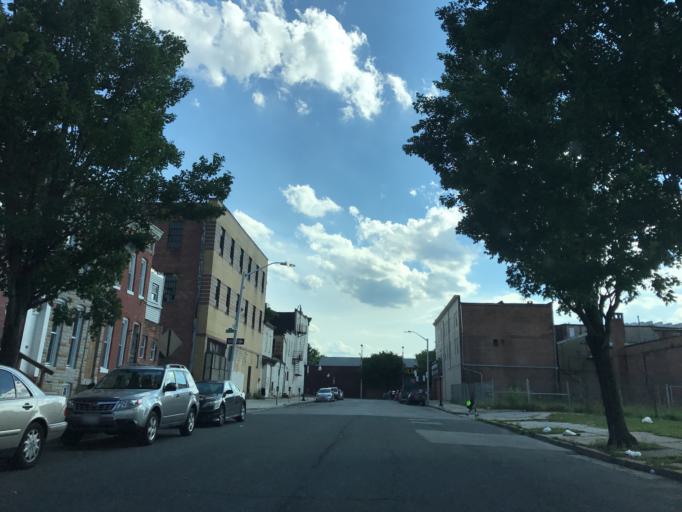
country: US
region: Maryland
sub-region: City of Baltimore
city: Baltimore
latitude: 39.3042
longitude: -76.6337
